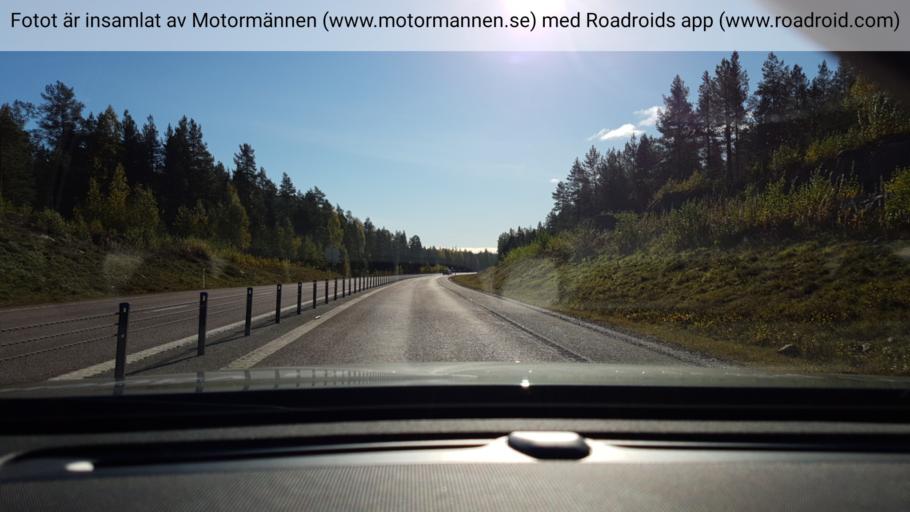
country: SE
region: Vaesterbotten
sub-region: Skelleftea Kommun
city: Burea
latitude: 64.6385
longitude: 21.1671
